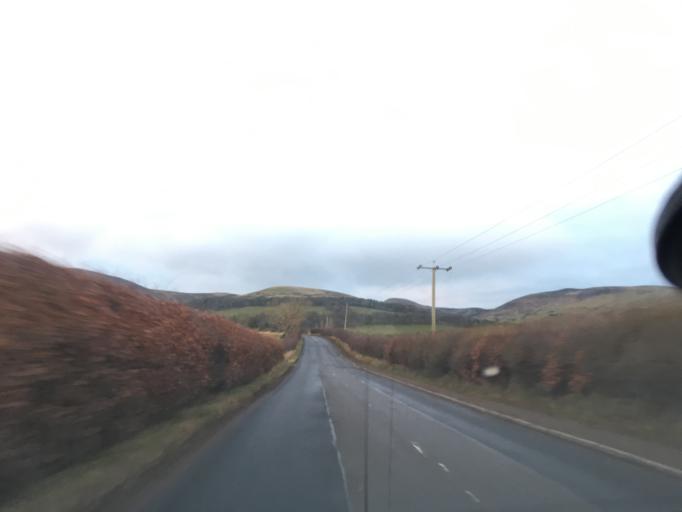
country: GB
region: Scotland
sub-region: Midlothian
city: Penicuik
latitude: 55.8637
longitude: -3.2070
